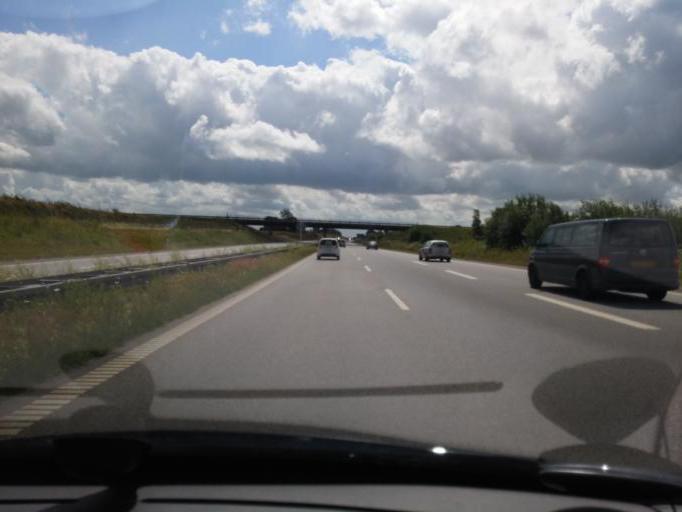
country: DK
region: South Denmark
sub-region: Odense Kommune
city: Hojby
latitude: 55.3420
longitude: 10.4537
